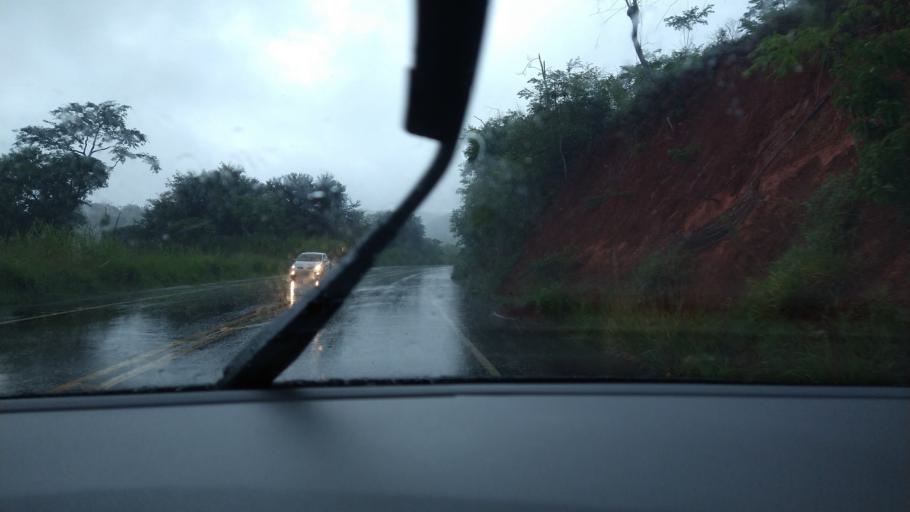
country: BR
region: Minas Gerais
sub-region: Ponte Nova
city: Ponte Nova
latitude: -20.5561
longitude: -42.8730
